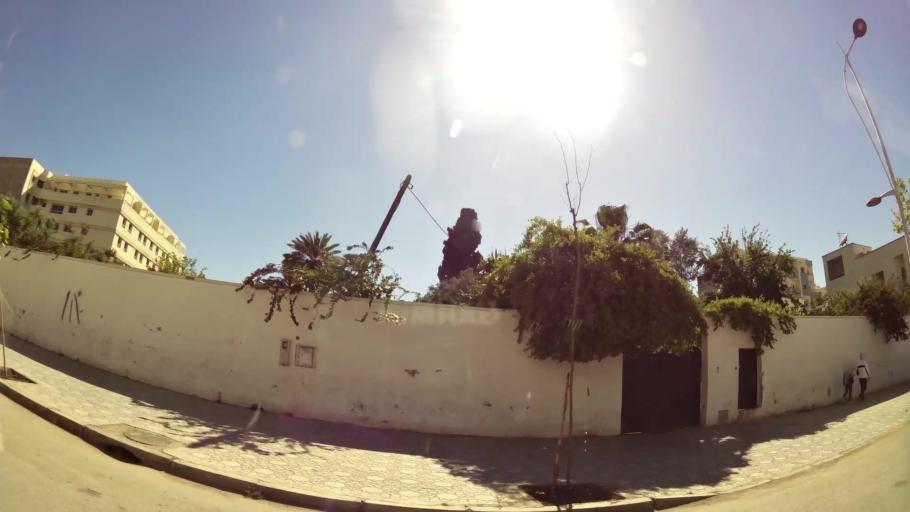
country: MA
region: Fes-Boulemane
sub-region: Fes
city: Fes
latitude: 34.0253
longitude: -4.9903
